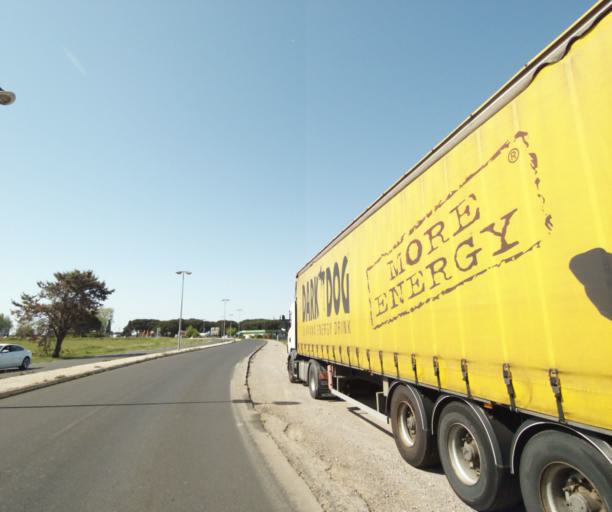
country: FR
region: Languedoc-Roussillon
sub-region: Departement de l'Herault
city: Perols
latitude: 43.5819
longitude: 3.9329
